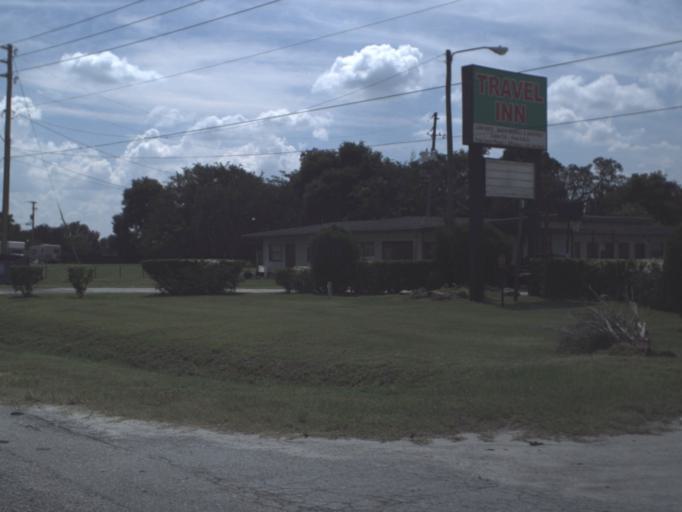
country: US
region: Florida
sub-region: Polk County
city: Lake Wales
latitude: 27.8891
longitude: -81.5999
